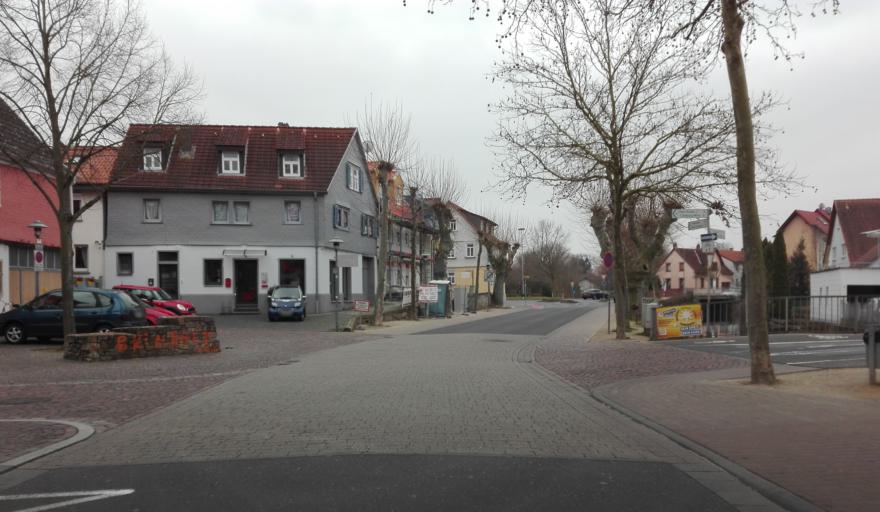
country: DE
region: Hesse
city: Dieburg
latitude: 49.8973
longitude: 8.8366
